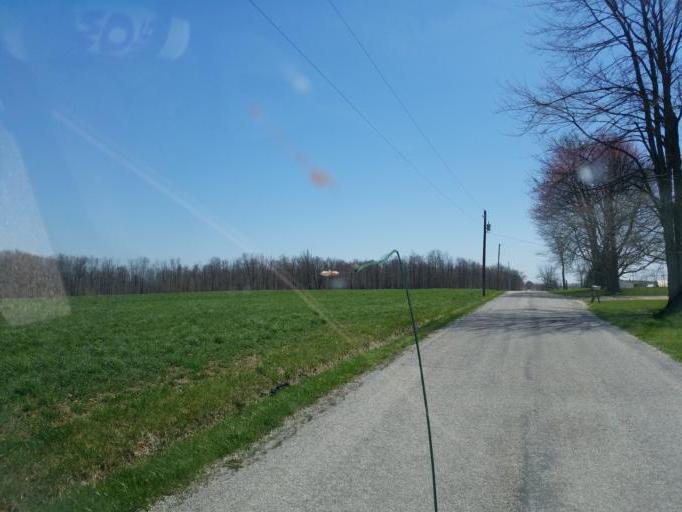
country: US
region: Ohio
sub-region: Huron County
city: Greenwich
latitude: 40.9848
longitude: -82.4569
